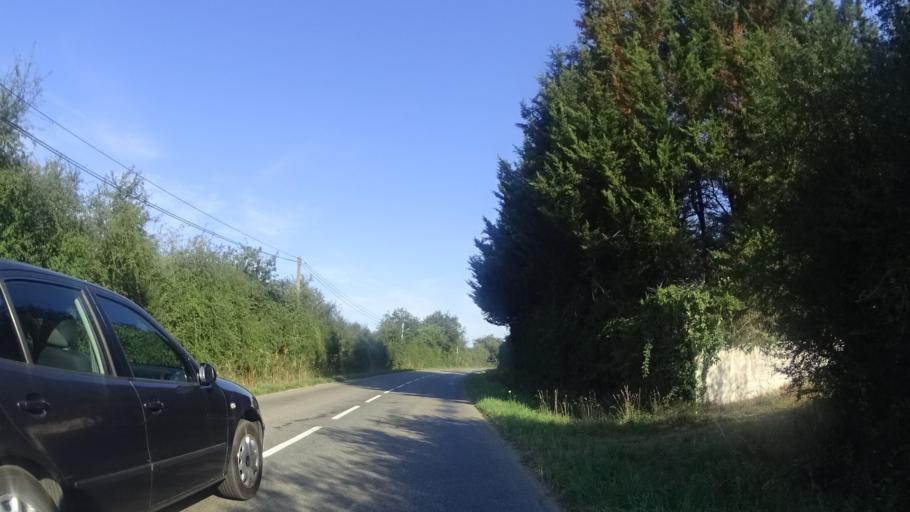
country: FR
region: Pays de la Loire
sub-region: Departement de la Loire-Atlantique
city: Joue-sur-Erdre
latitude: 47.4921
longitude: -1.4132
